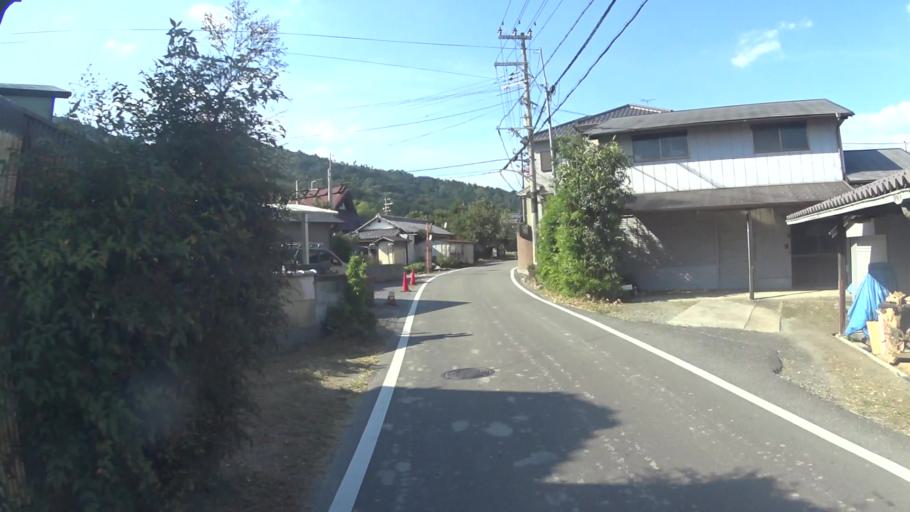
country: JP
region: Kyoto
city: Kameoka
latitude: 35.0282
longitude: 135.5432
